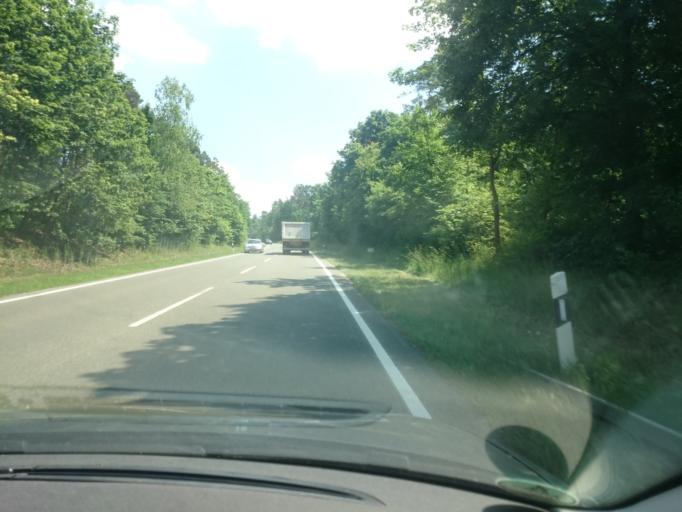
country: DE
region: Bavaria
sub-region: Regierungsbezirk Mittelfranken
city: Hilpoltstein
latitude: 49.2091
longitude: 11.1562
